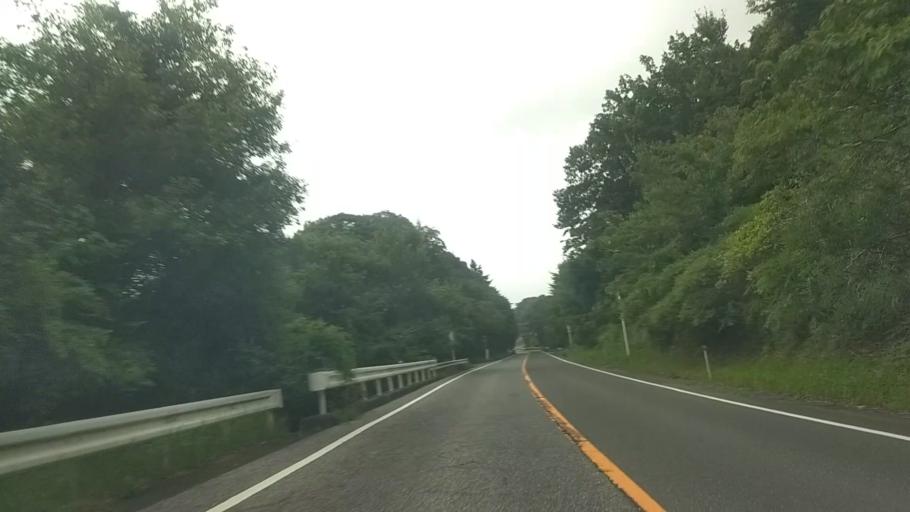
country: JP
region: Chiba
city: Kawaguchi
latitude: 35.2191
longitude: 140.0385
